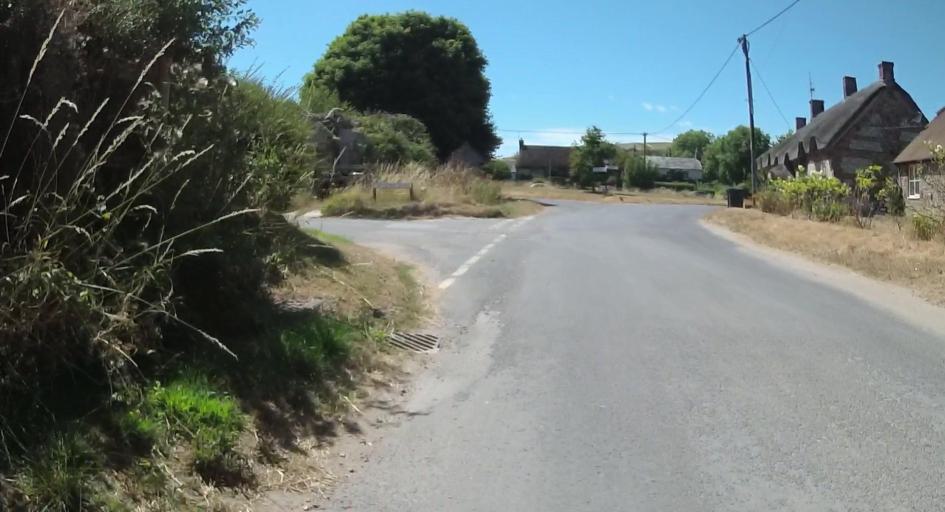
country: GB
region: England
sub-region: Dorset
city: Bovington Camp
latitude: 50.6498
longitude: -2.2960
